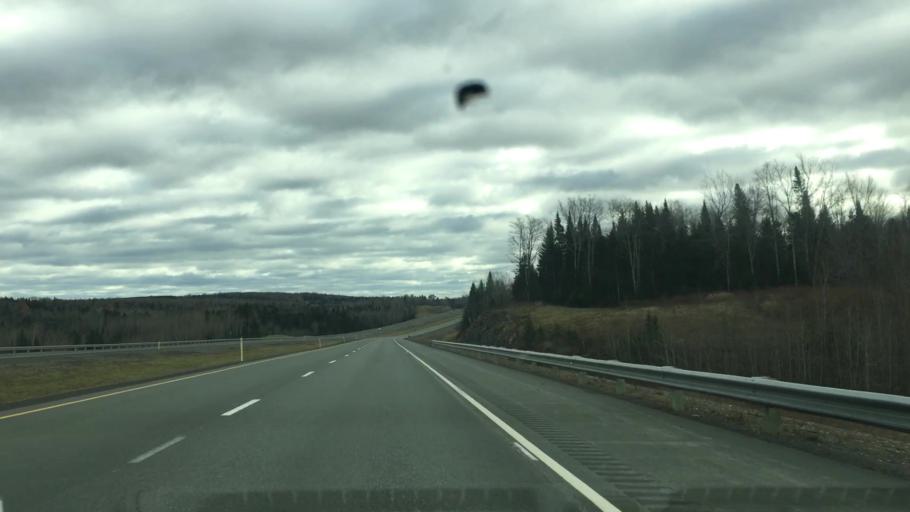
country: CA
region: New Brunswick
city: Florenceville-Bristol
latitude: 46.5435
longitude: -67.7184
